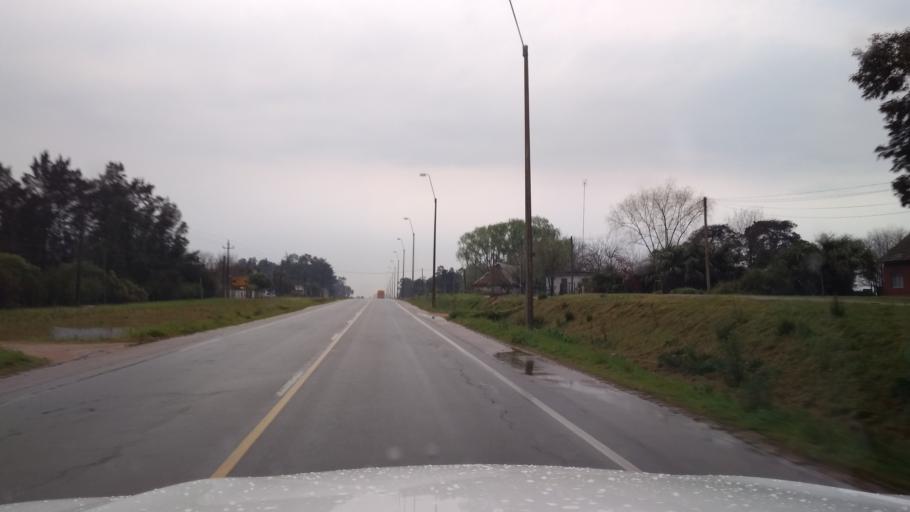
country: UY
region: Canelones
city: Toledo
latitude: -34.7634
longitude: -56.1183
